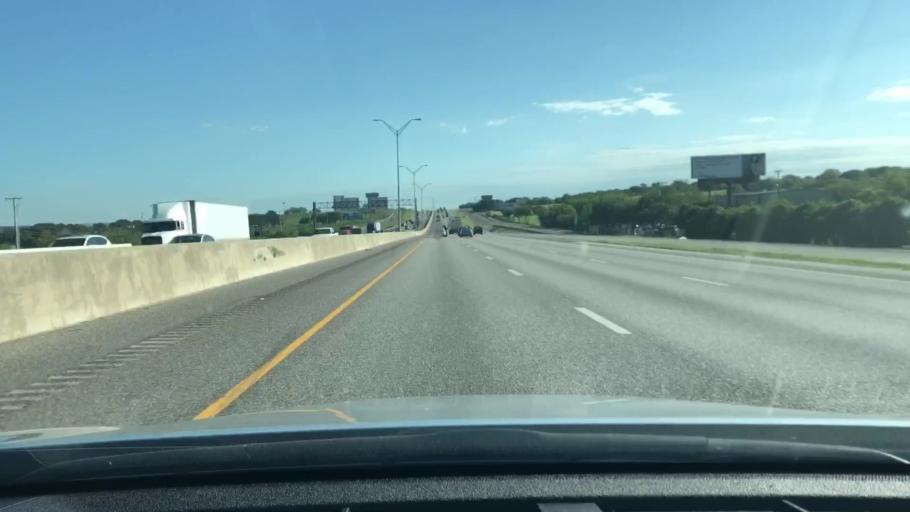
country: US
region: Texas
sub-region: Guadalupe County
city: Northcliff
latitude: 29.6262
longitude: -98.2379
